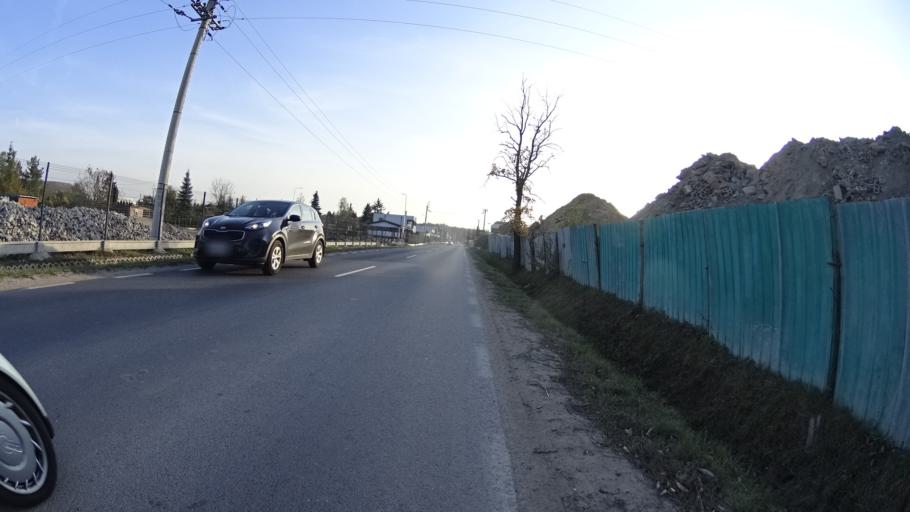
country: PL
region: Masovian Voivodeship
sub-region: Powiat warszawski zachodni
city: Babice
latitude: 52.2816
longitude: 20.8668
